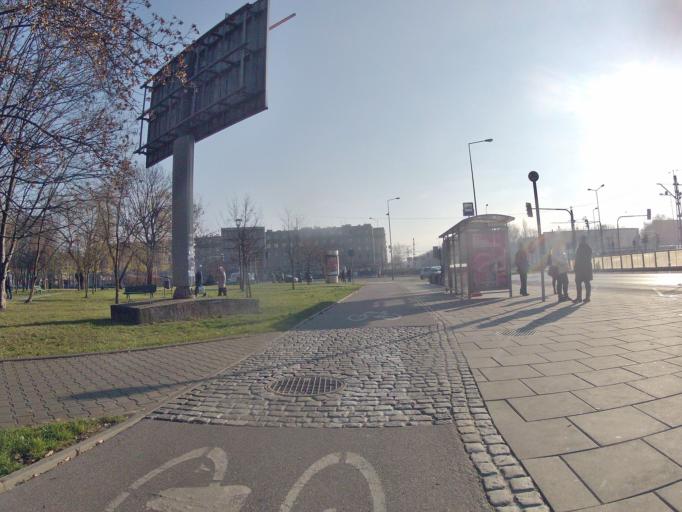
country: PL
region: Lesser Poland Voivodeship
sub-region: Powiat wielicki
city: Kokotow
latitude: 50.0806
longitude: 20.0266
